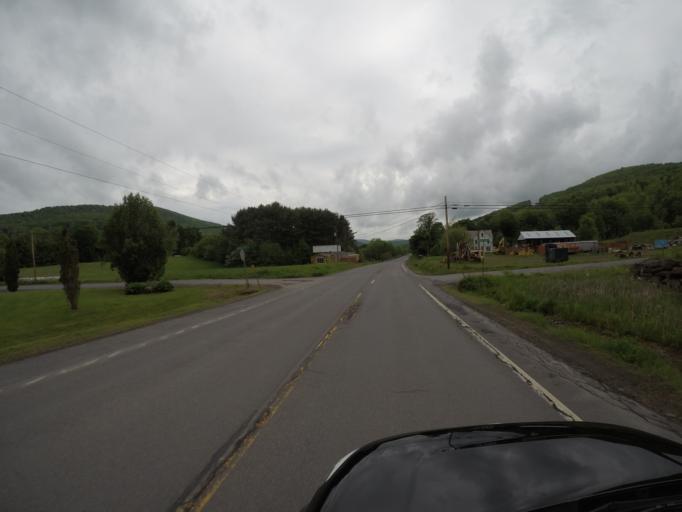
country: US
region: New York
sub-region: Delaware County
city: Delhi
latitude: 42.2546
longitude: -74.9027
